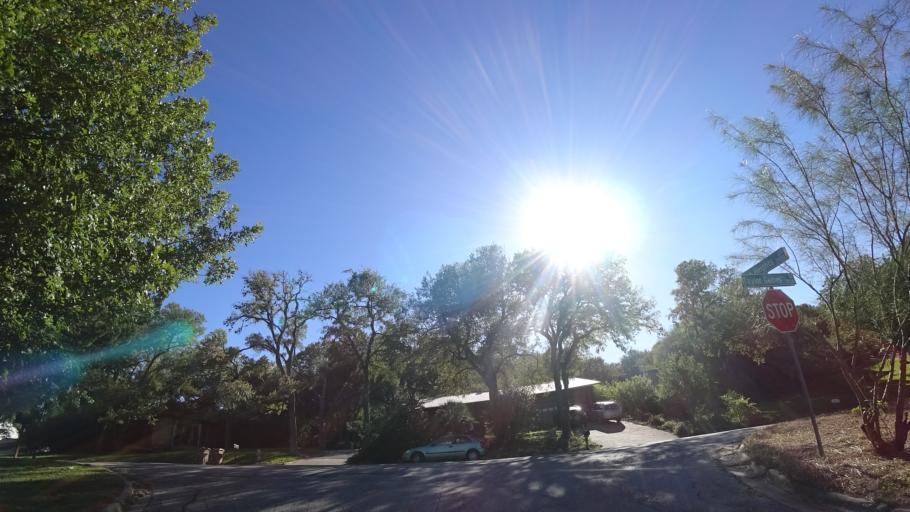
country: US
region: Texas
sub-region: Travis County
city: Austin
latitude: 30.2407
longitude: -97.7338
